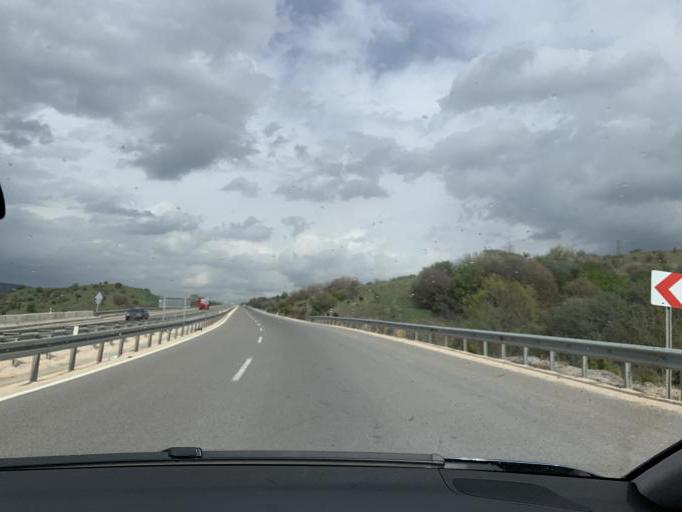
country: TR
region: Bolu
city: Yenicaga
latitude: 40.7804
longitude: 32.0931
